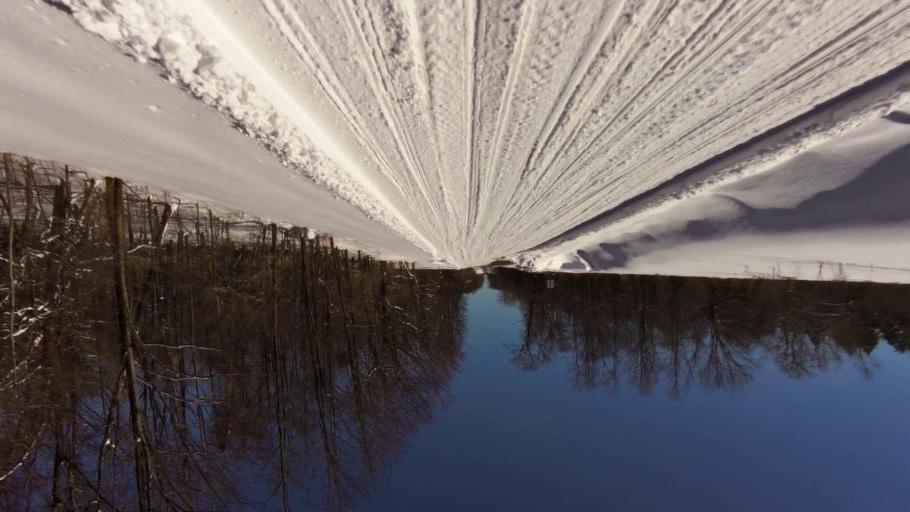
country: US
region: New York
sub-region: Chautauqua County
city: Mayville
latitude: 42.2176
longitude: -79.5339
